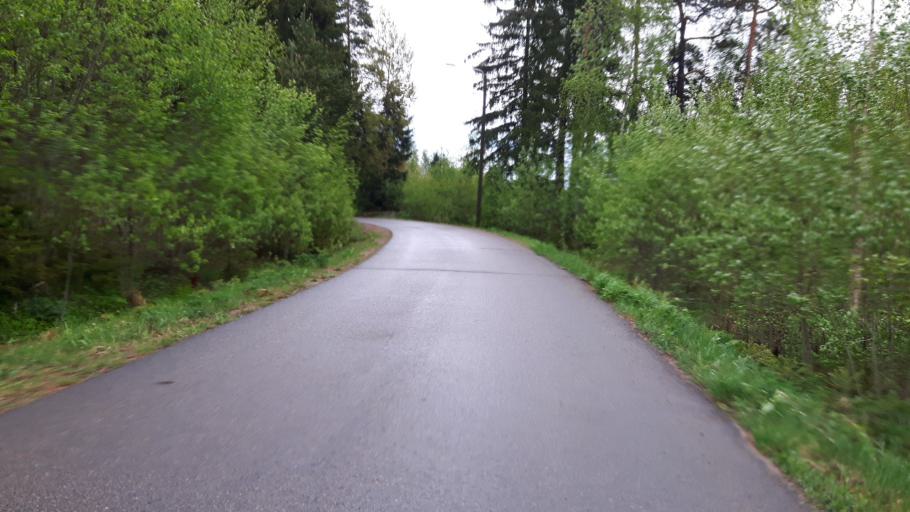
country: FI
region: Kymenlaakso
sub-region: Kotka-Hamina
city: Karhula
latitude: 60.5597
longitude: 27.0255
